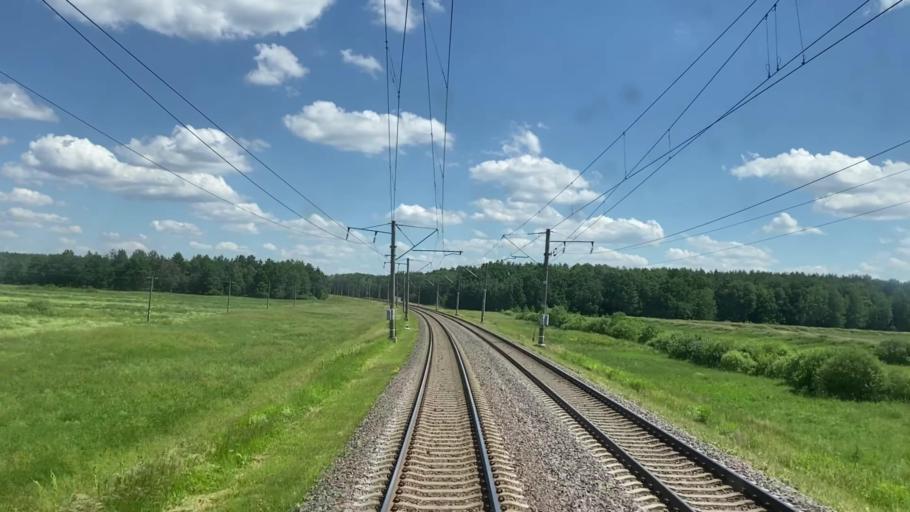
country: BY
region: Brest
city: Ivatsevichy
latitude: 52.8421
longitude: 25.5504
